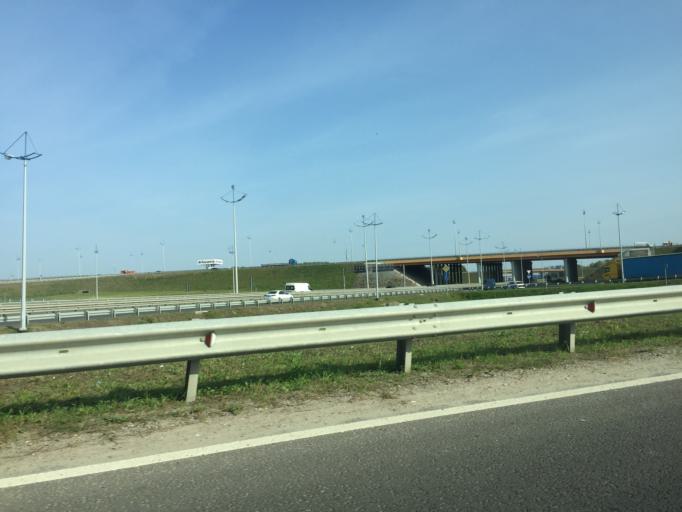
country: RU
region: Kaliningrad
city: Bol'shoe Isakovo
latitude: 54.7041
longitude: 20.5945
